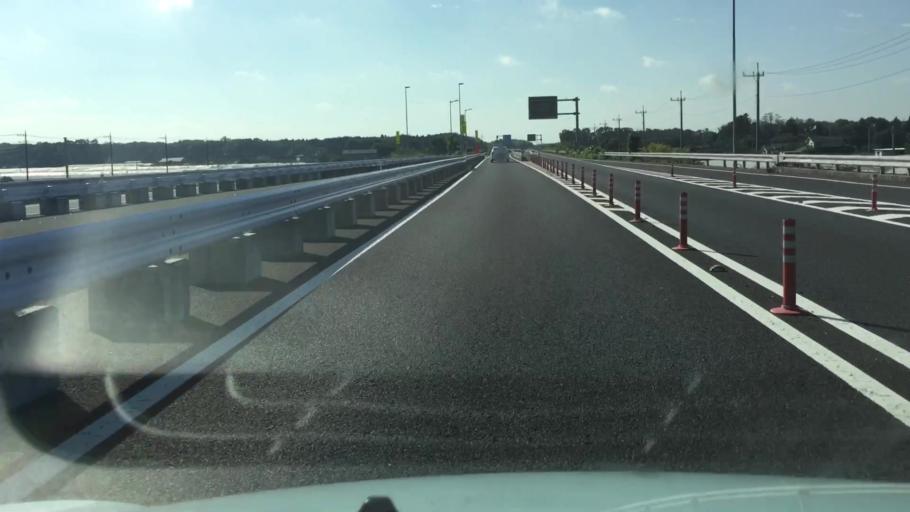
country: JP
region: Tochigi
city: Mooka
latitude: 36.5083
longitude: 139.9874
